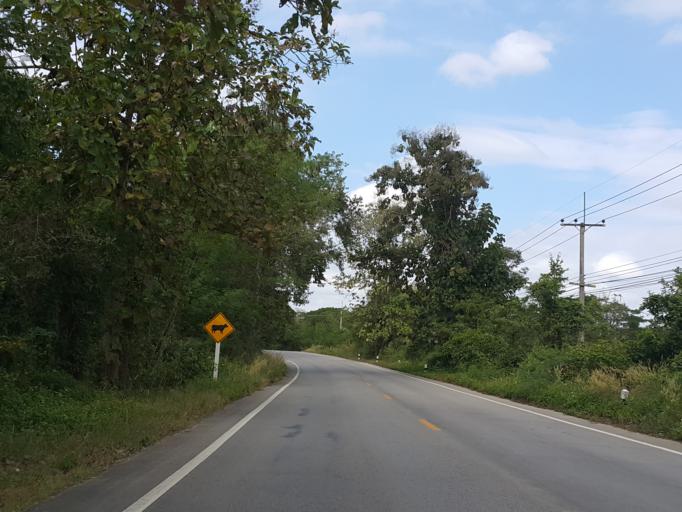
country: TH
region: Lampang
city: Lampang
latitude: 18.4156
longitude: 99.4496
